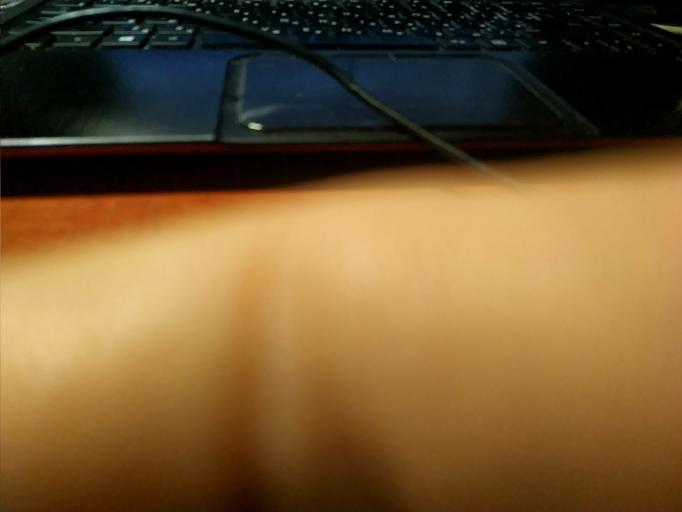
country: RU
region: Vologda
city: Vytegra
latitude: 60.8075
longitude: 36.7463
